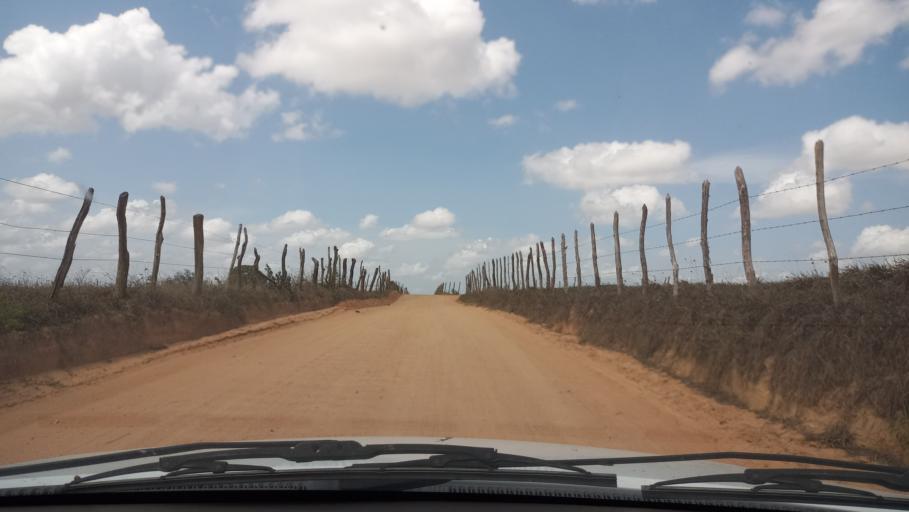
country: BR
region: Rio Grande do Norte
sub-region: Montanhas
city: Montanhas
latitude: -6.3543
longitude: -35.3351
